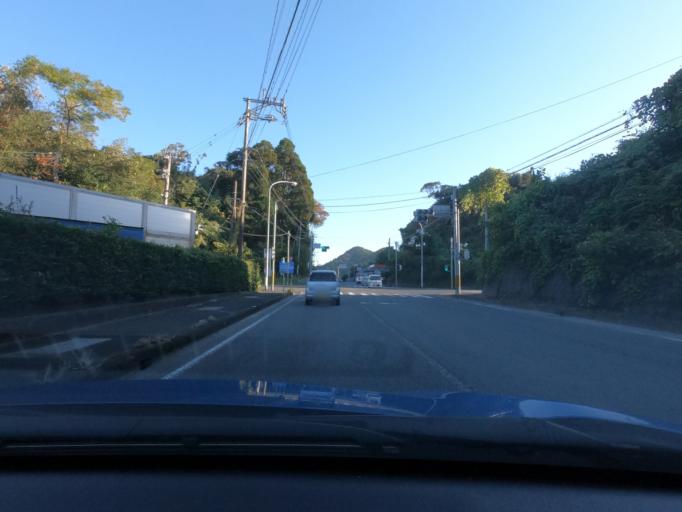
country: JP
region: Kagoshima
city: Satsumasendai
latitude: 31.8585
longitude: 130.2315
